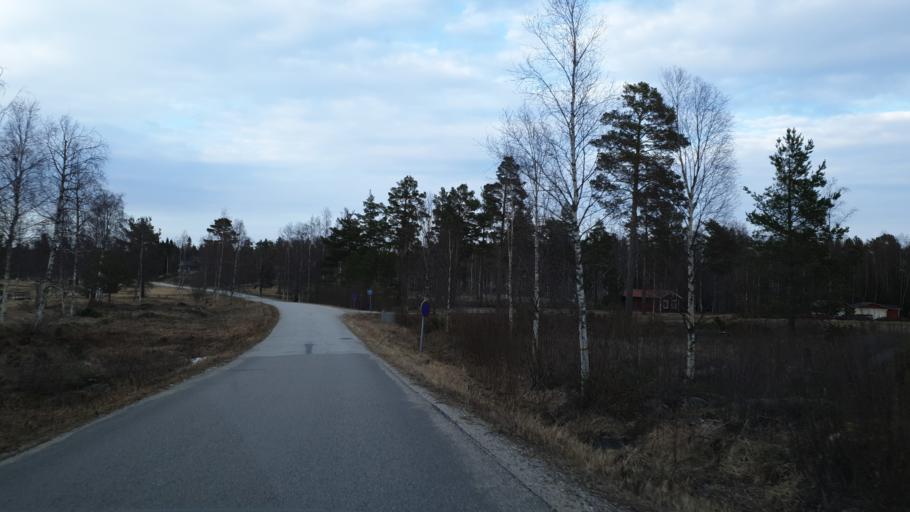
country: SE
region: Vaesternorrland
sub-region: Sundsvalls Kommun
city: Njurundabommen
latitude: 62.0183
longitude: 17.4057
